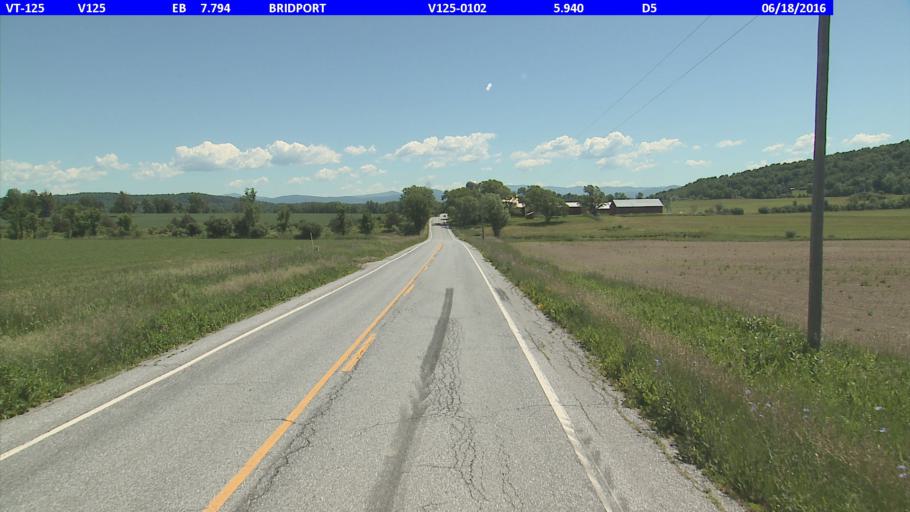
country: US
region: Vermont
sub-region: Addison County
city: Middlebury (village)
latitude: 43.9899
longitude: -73.2989
